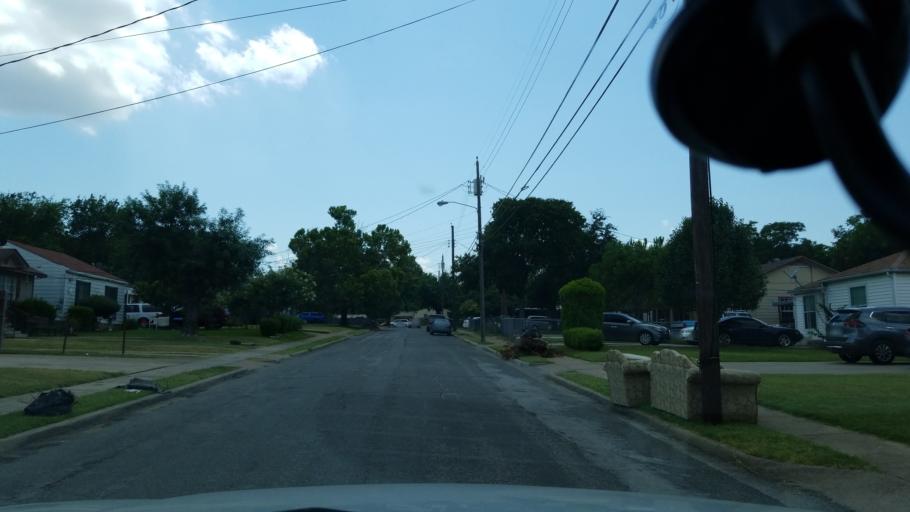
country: US
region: Texas
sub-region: Dallas County
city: Cockrell Hill
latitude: 32.7302
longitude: -96.8805
